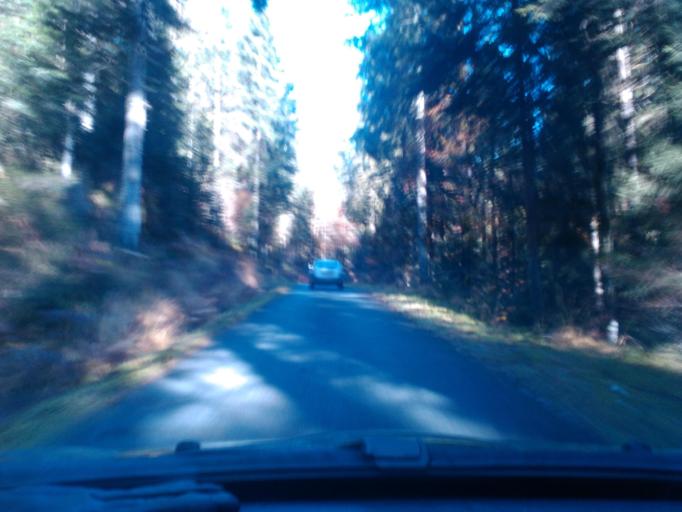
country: FR
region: Lorraine
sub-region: Departement des Vosges
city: Senones
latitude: 48.4565
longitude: 7.0568
